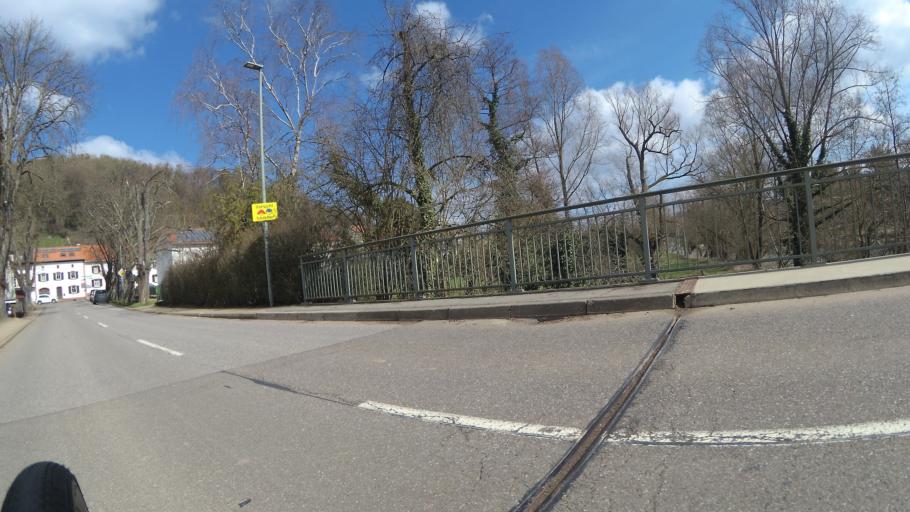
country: DE
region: Saarland
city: Rehlingen-Siersburg
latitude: 49.3570
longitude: 6.6158
